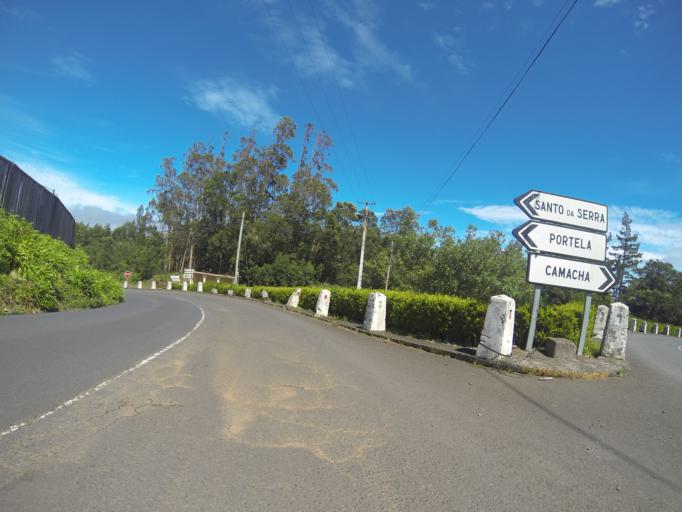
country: PT
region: Madeira
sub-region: Santa Cruz
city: Camacha
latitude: 32.7177
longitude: -16.8329
